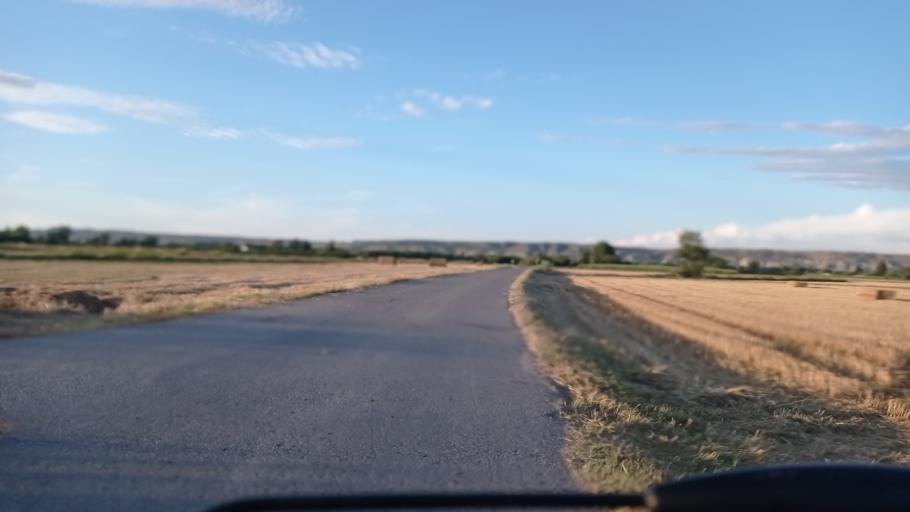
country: ES
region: Aragon
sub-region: Provincia de Zaragoza
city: Oliver-Valdefierro, Oliver, Valdefierro
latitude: 41.6820
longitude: -0.9374
